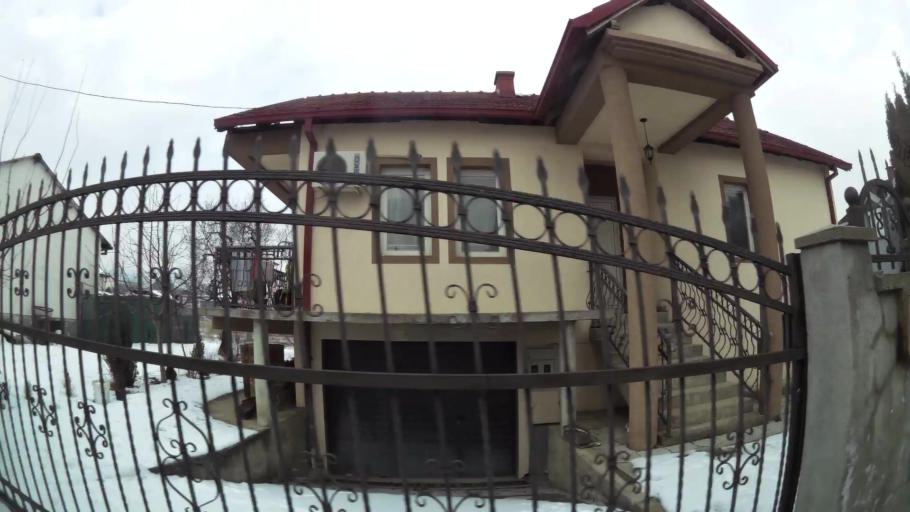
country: MK
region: Saraj
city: Saraj
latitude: 42.0238
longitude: 21.3521
